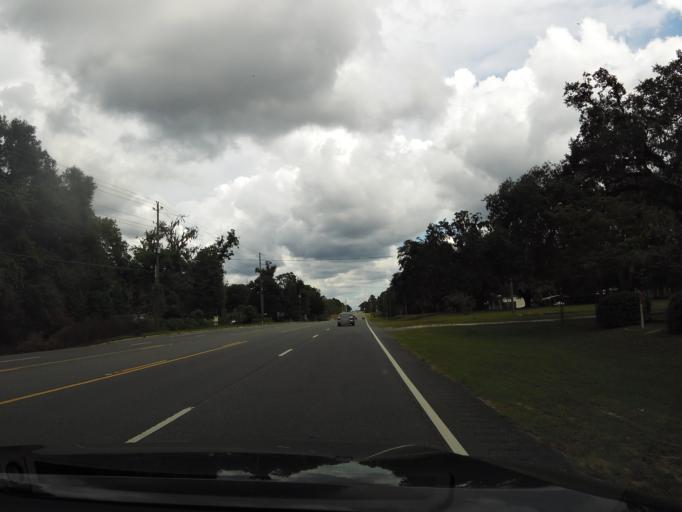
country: US
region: Georgia
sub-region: Brantley County
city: Nahunta
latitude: 31.2299
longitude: -81.7823
